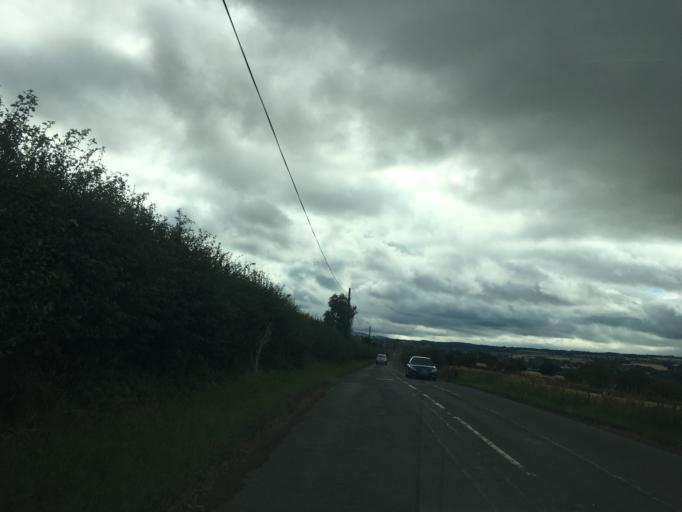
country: GB
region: Scotland
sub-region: Midlothian
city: Gorebridge
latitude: 55.8612
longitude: -3.0550
